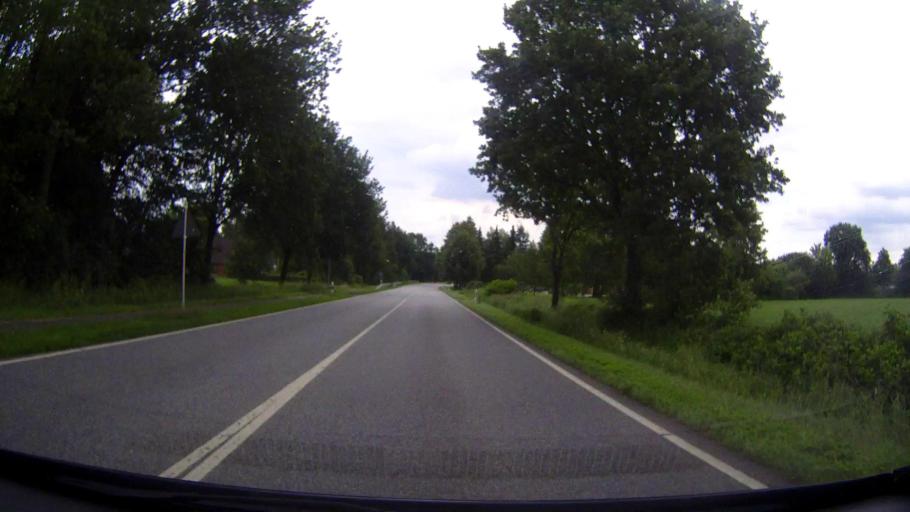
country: DE
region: Schleswig-Holstein
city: Reher
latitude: 54.0666
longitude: 9.5641
